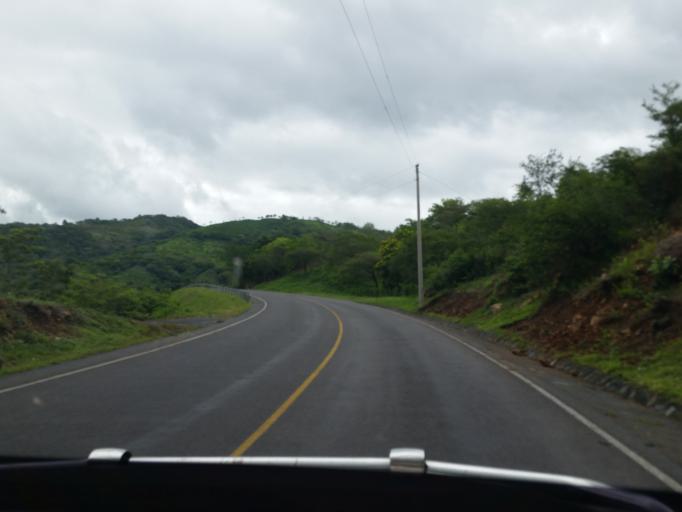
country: NI
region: Matagalpa
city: Matagalpa
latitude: 12.9763
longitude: -86.0306
